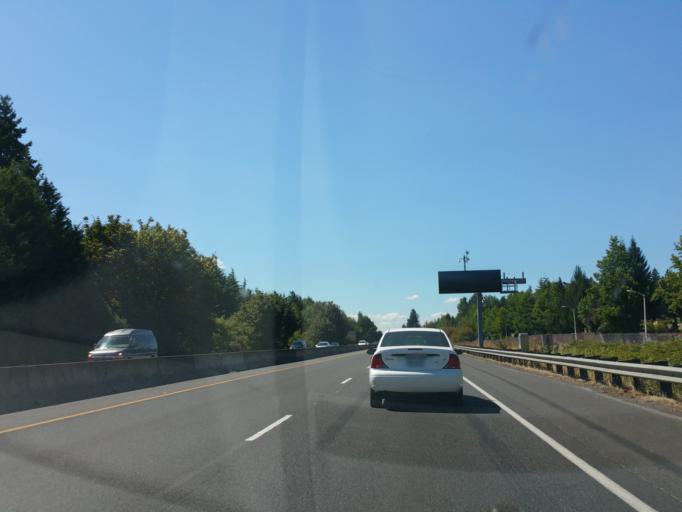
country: US
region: Washington
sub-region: Clark County
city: Mill Plain
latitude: 45.5958
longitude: -122.5189
